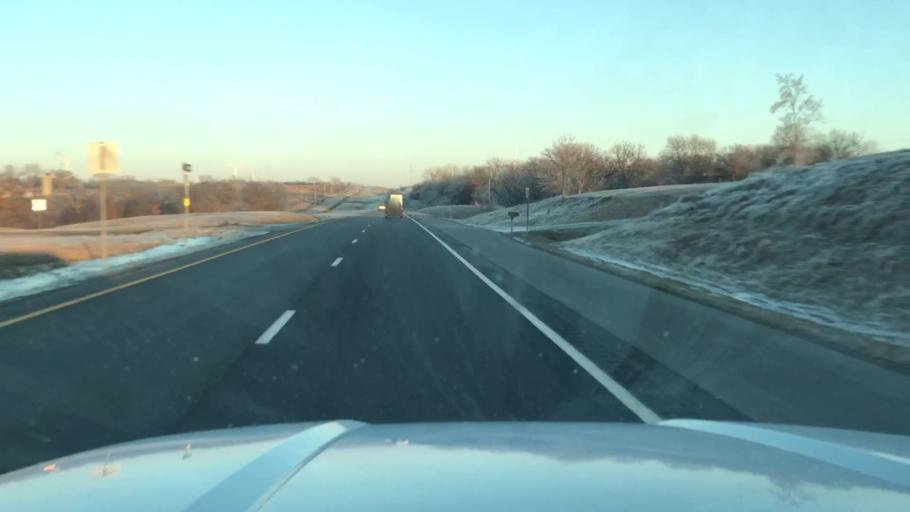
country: US
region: Missouri
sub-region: DeKalb County
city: Maysville
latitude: 39.7620
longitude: -94.4621
